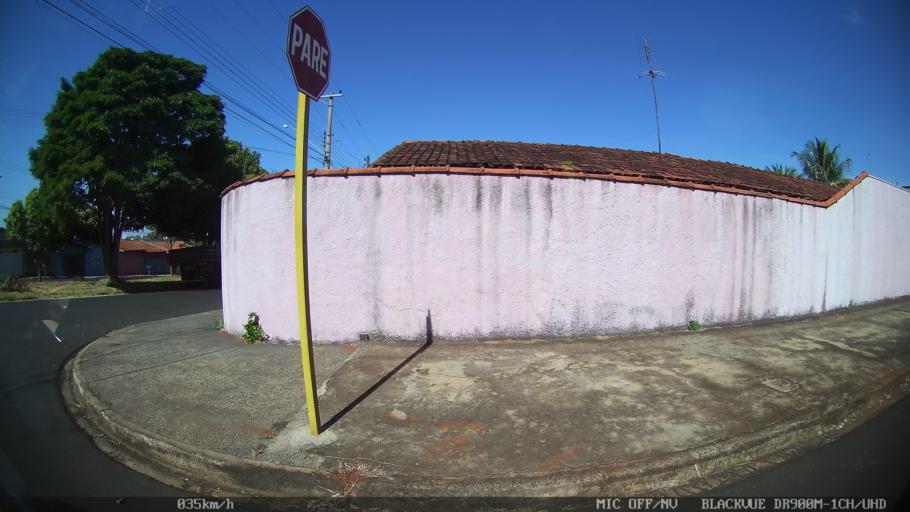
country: BR
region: Sao Paulo
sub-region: Batatais
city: Batatais
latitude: -20.8889
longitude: -47.5732
